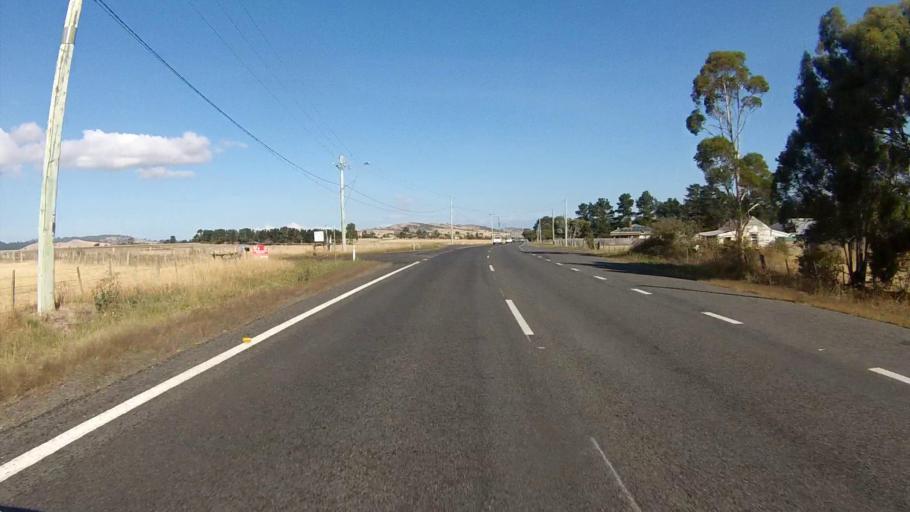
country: AU
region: Tasmania
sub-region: Sorell
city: Sorell
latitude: -42.7303
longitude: 147.5267
